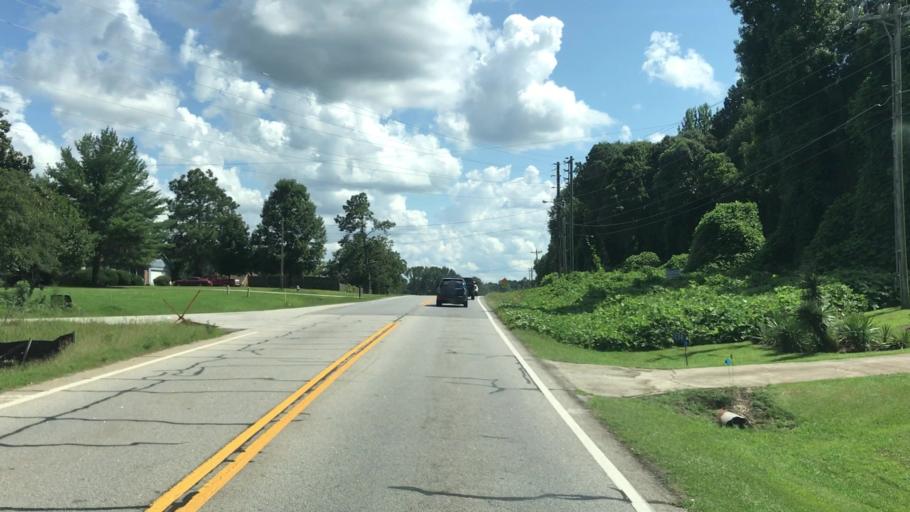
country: US
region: Georgia
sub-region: Walton County
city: Walnut Grove
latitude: 33.7610
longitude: -83.8512
